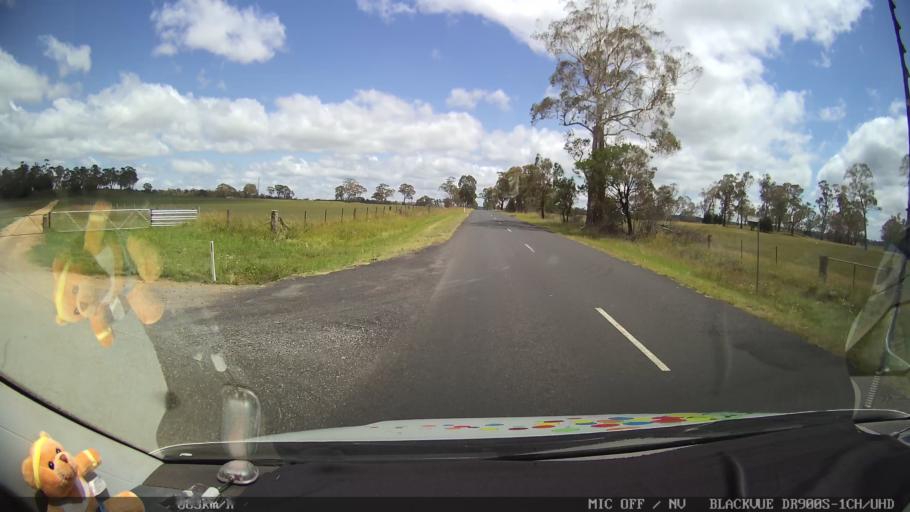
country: AU
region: New South Wales
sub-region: Glen Innes Severn
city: Glen Innes
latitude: -29.6244
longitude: 151.6709
